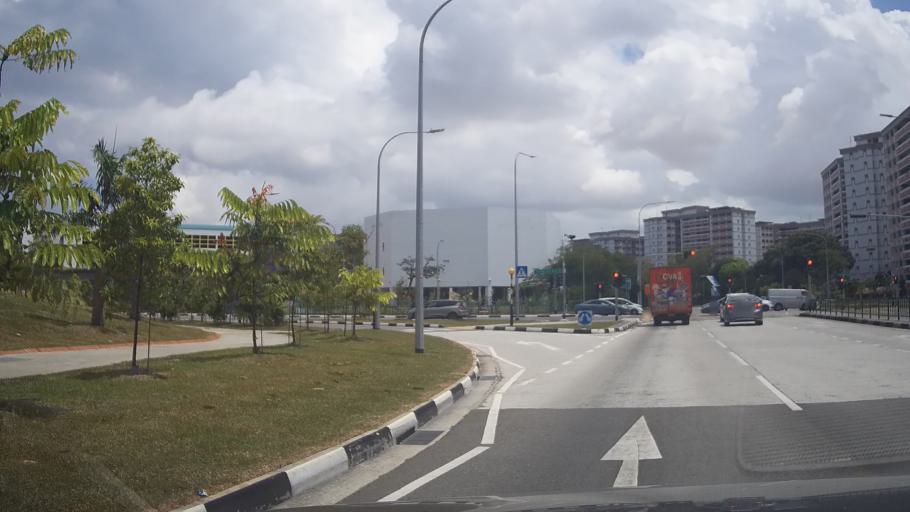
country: SG
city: Singapore
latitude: 1.3563
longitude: 103.9548
